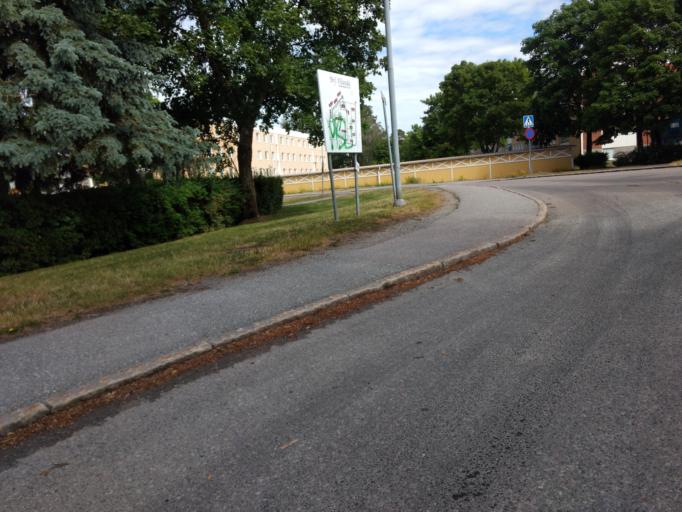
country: SE
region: Stockholm
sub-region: Upplands Vasby Kommun
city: Upplands Vaesby
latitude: 59.5215
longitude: 17.9161
